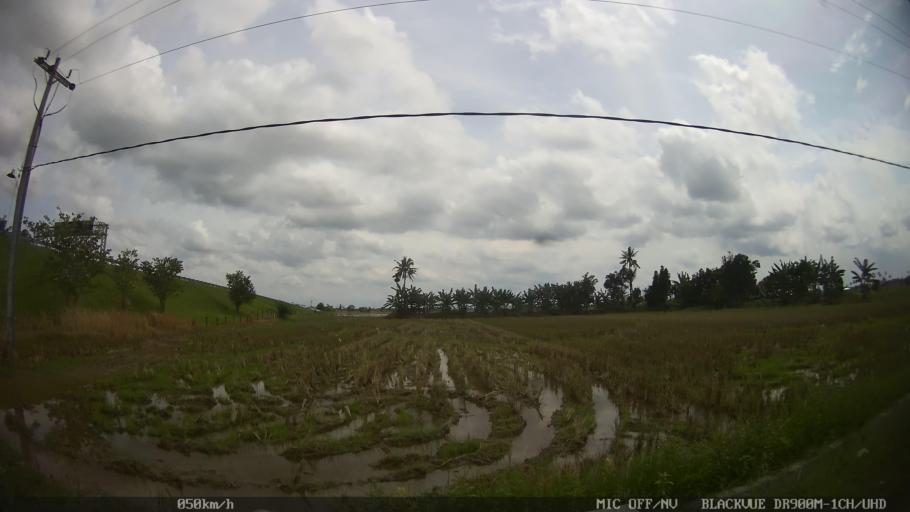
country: ID
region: North Sumatra
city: Percut
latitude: 3.5721
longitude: 98.8468
